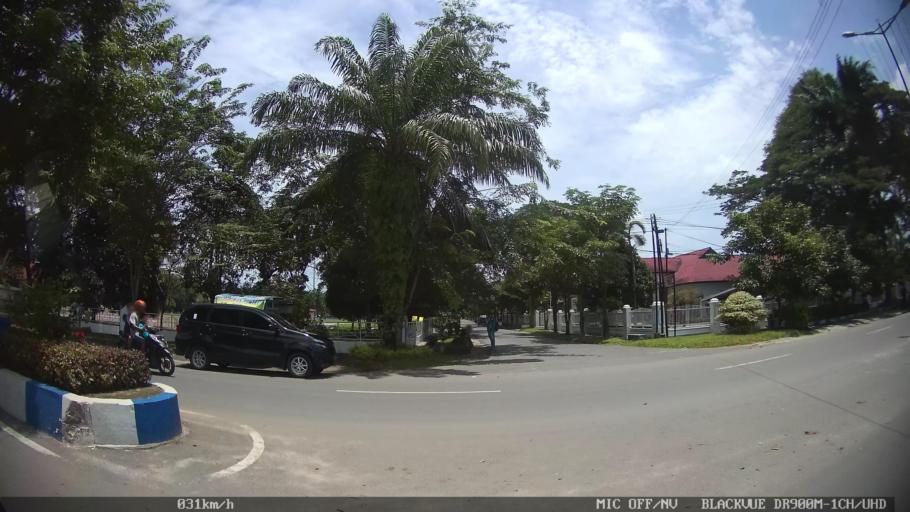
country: ID
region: North Sumatra
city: Percut
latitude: 3.5482
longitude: 98.8654
